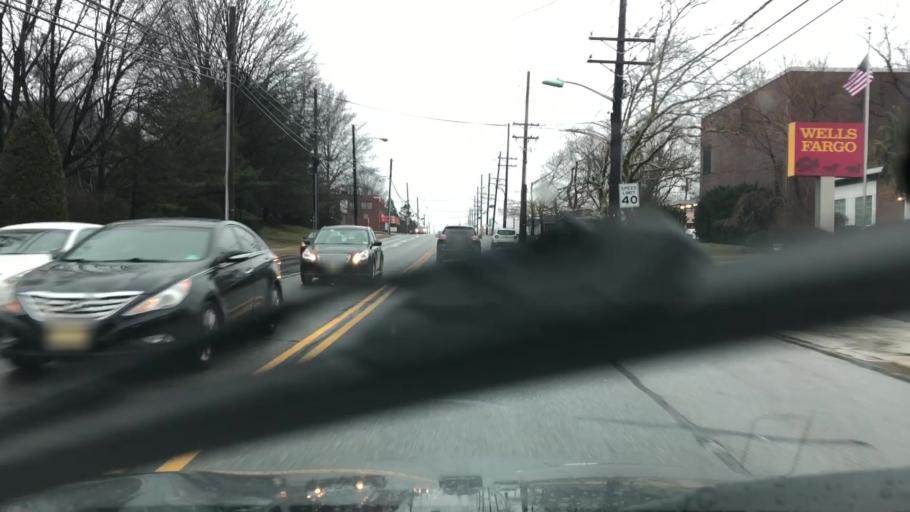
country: US
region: New Jersey
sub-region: Middlesex County
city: Edison
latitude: 40.5166
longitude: -74.4007
